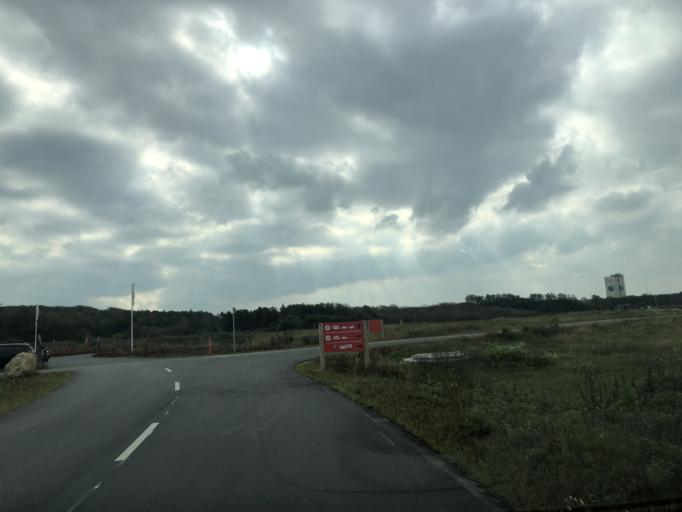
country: DK
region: Central Jutland
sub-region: Ringkobing-Skjern Kommune
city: Ringkobing
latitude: 56.1030
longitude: 8.2457
